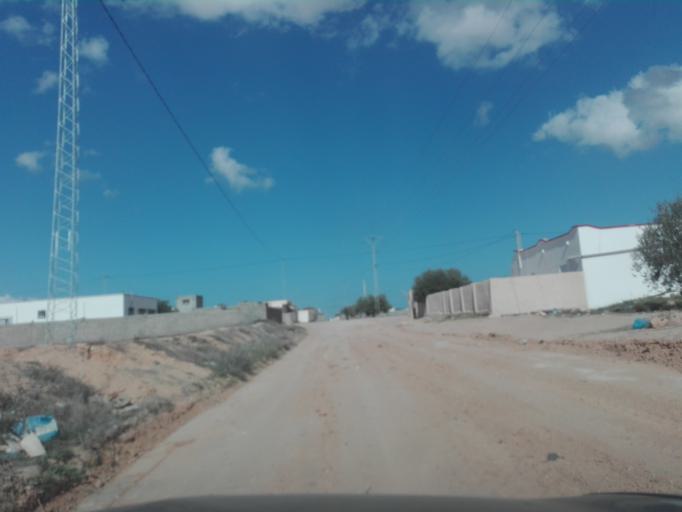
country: TN
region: Madanin
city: Bin Qirdan
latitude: 33.1523
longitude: 11.1930
